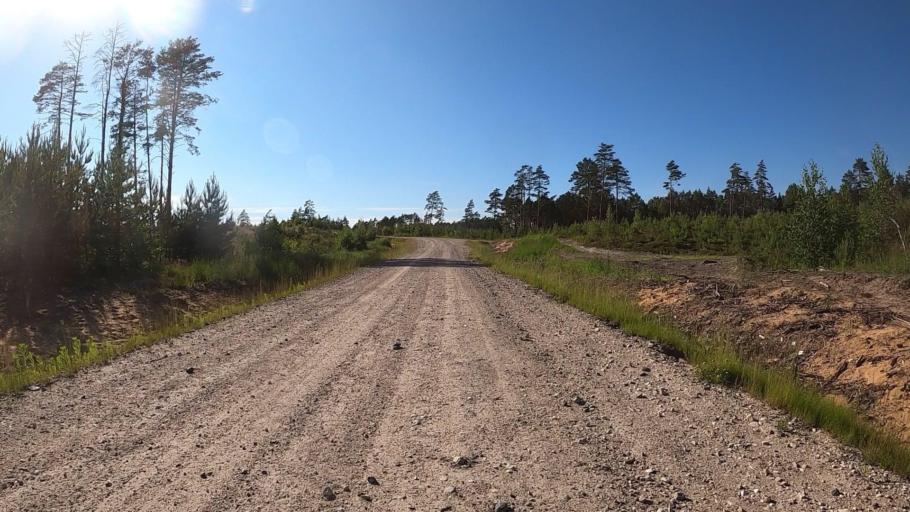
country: LV
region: Carnikava
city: Carnikava
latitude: 57.0943
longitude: 24.2452
